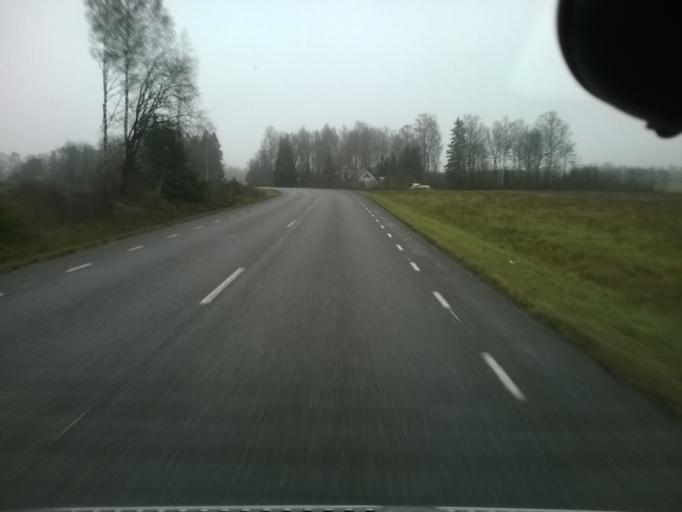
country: EE
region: Raplamaa
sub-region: Kohila vald
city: Kohila
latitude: 59.1495
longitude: 24.6166
